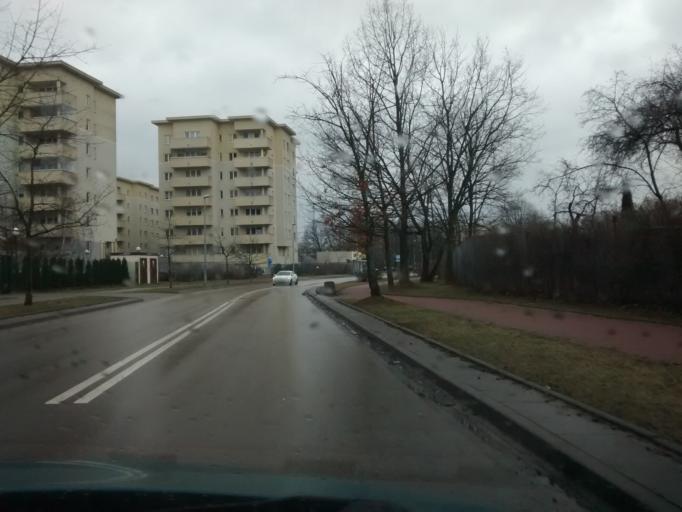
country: PL
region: Masovian Voivodeship
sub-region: Warszawa
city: Bialoleka
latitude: 52.3233
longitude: 20.9620
